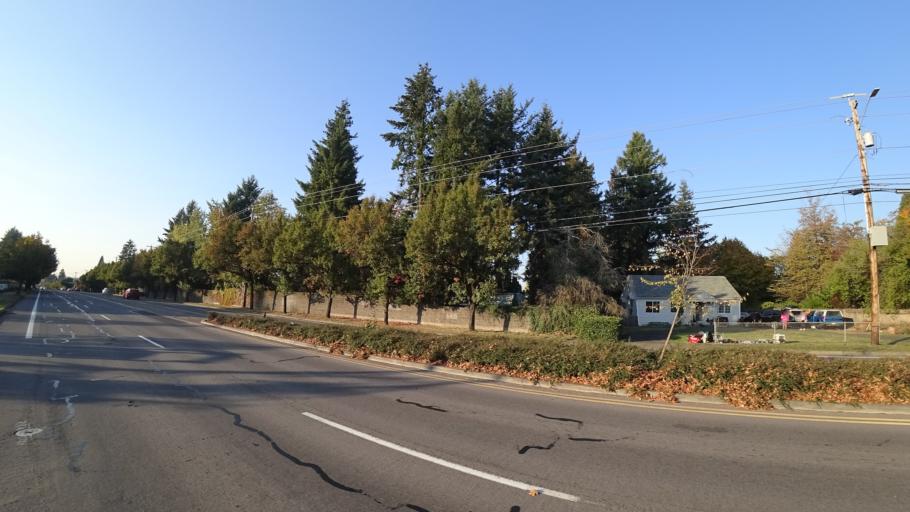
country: US
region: Oregon
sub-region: Multnomah County
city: Gresham
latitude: 45.5116
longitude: -122.4413
